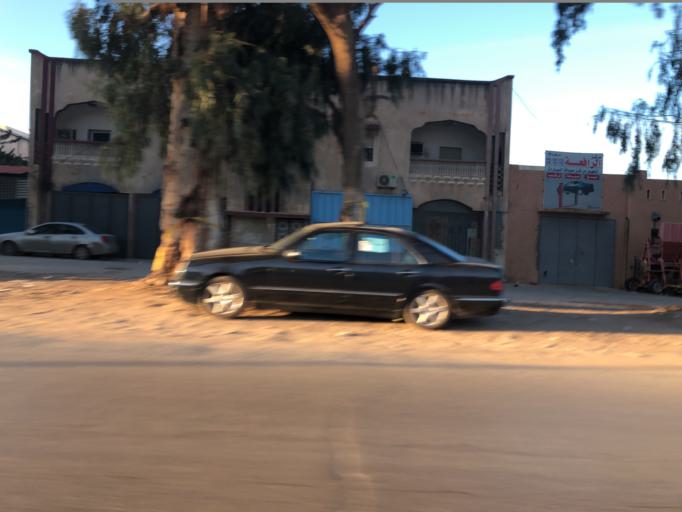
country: LY
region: Tripoli
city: Tagiura
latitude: 32.8699
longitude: 13.2956
